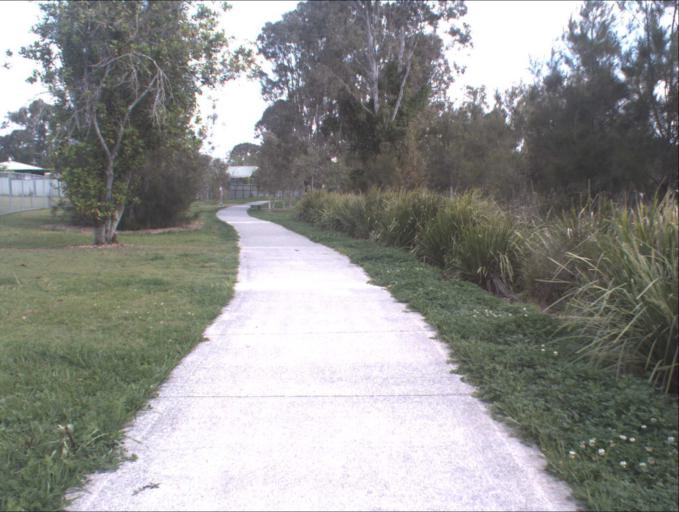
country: AU
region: Queensland
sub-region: Logan
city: Waterford West
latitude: -27.6947
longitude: 153.1350
